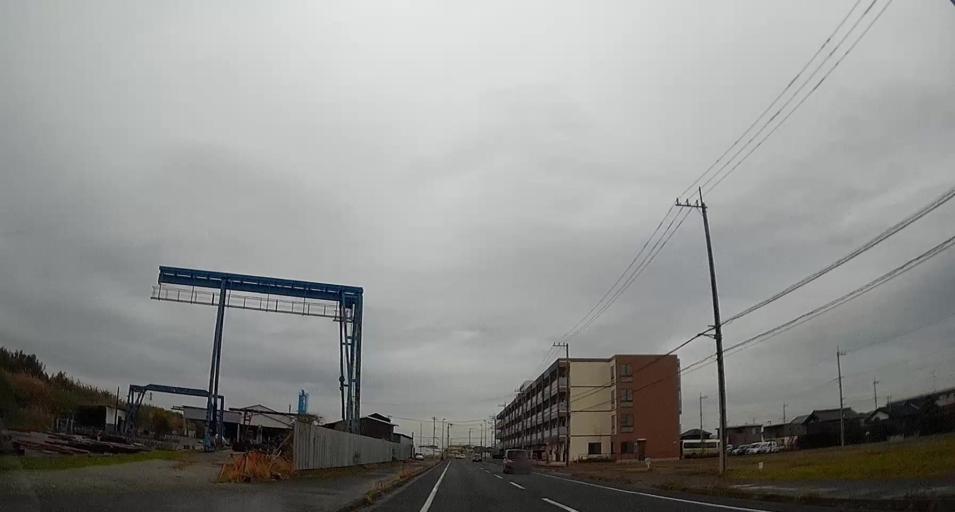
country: JP
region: Chiba
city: Kisarazu
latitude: 35.4279
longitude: 139.9384
